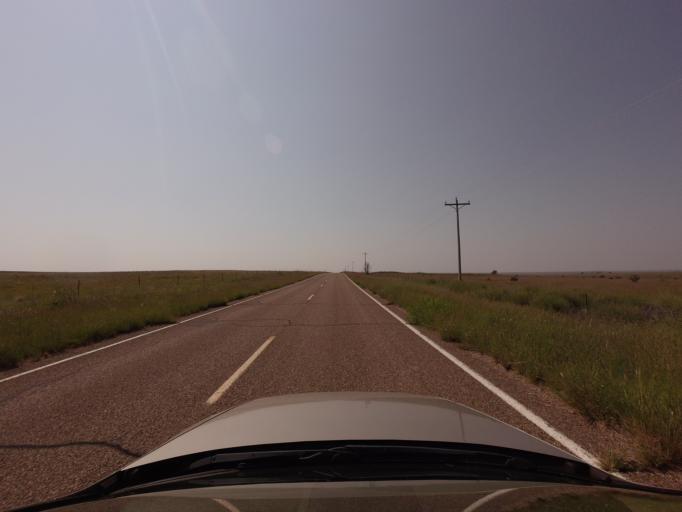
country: US
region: New Mexico
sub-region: Curry County
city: Cannon Air Force Base
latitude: 34.6757
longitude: -103.6356
